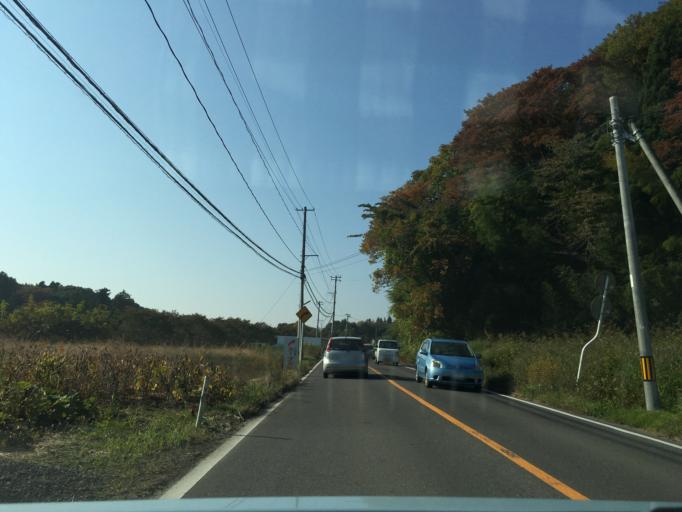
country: JP
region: Fukushima
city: Sukagawa
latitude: 37.2830
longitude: 140.3323
